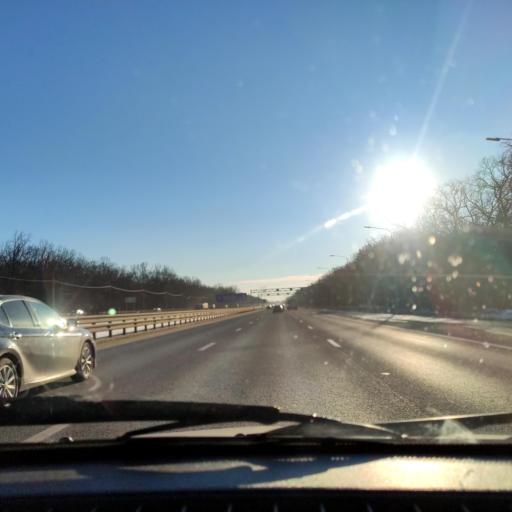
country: RU
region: Voronezj
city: Podgornoye
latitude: 51.7698
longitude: 39.1916
